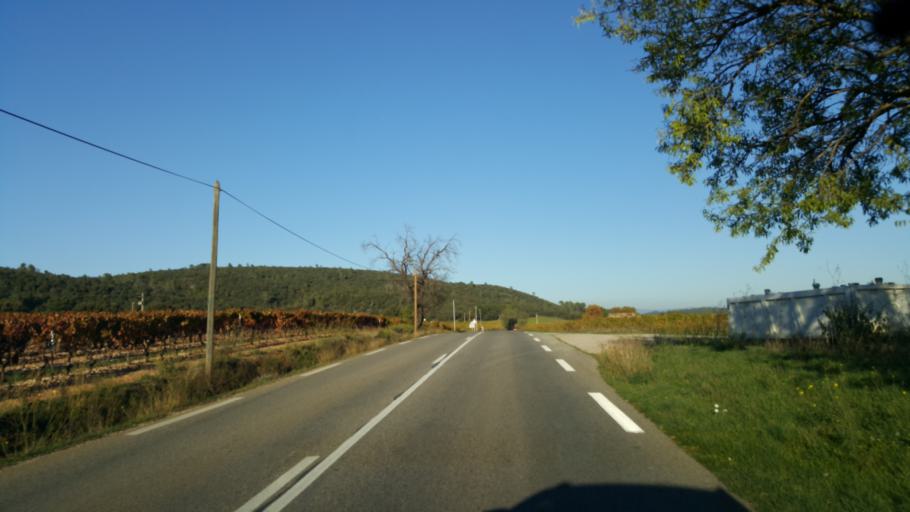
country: FR
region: Provence-Alpes-Cote d'Azur
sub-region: Departement du Var
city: Saint-Maximin-la-Sainte-Baume
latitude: 43.4982
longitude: 5.8991
